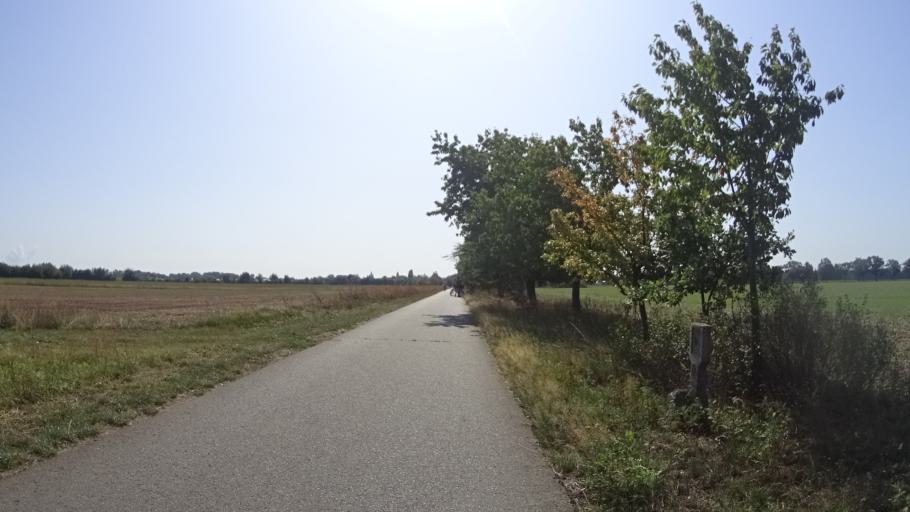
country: DE
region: Brandenburg
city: Werben
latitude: 51.8203
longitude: 14.1675
